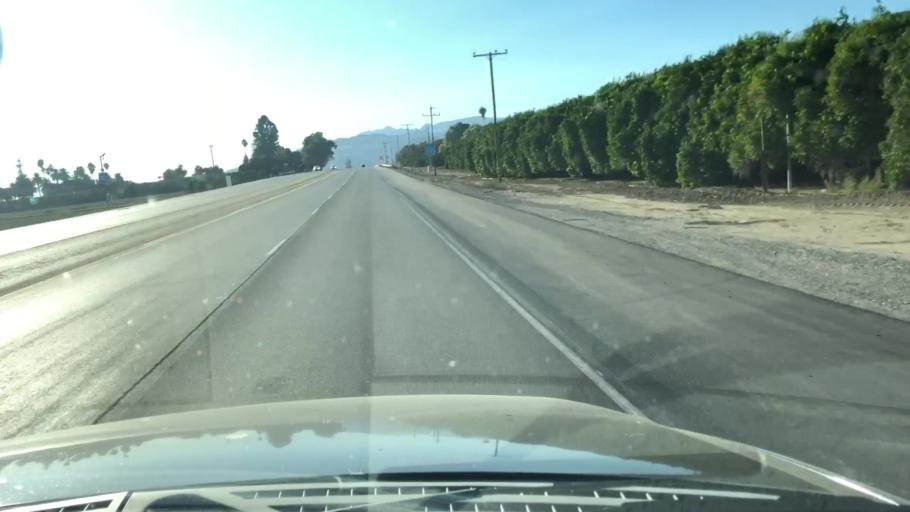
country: US
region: California
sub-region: Ventura County
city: Piru
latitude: 34.4083
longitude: -118.7524
